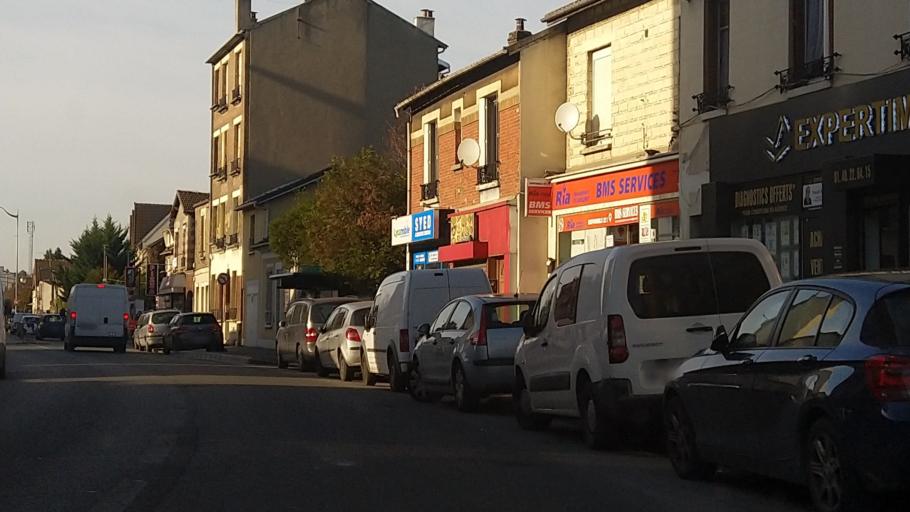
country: FR
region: Ile-de-France
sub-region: Departement de Seine-Saint-Denis
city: Stains
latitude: 48.9625
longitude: 2.3795
